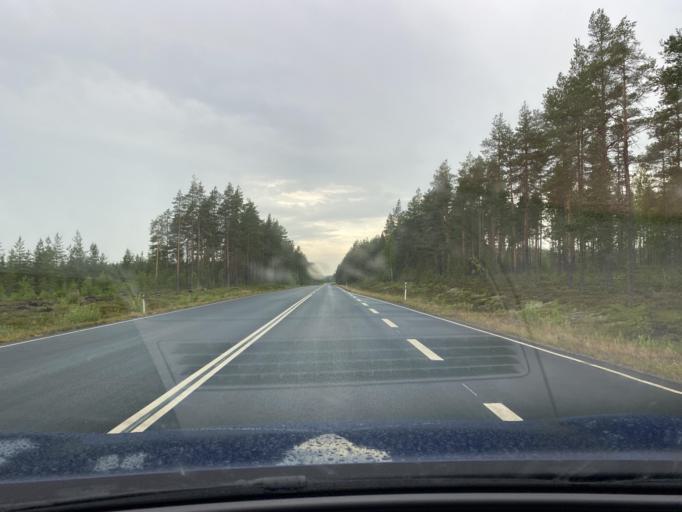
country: FI
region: Central Ostrobothnia
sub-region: Kaustinen
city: Halsua
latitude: 63.4083
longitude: 23.9761
